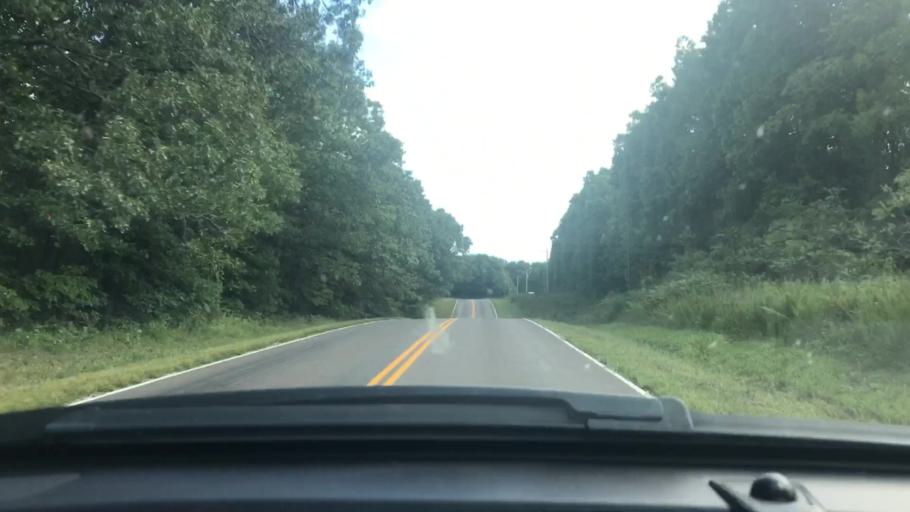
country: US
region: Missouri
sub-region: Wright County
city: Hartville
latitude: 37.3578
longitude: -92.3424
